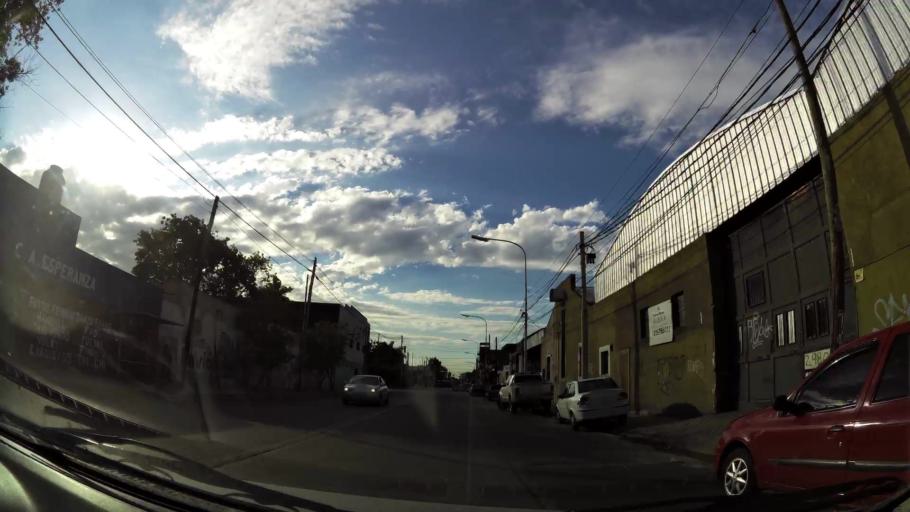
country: AR
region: Buenos Aires
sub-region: Partido de Avellaneda
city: Avellaneda
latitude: -34.6894
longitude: -58.3552
